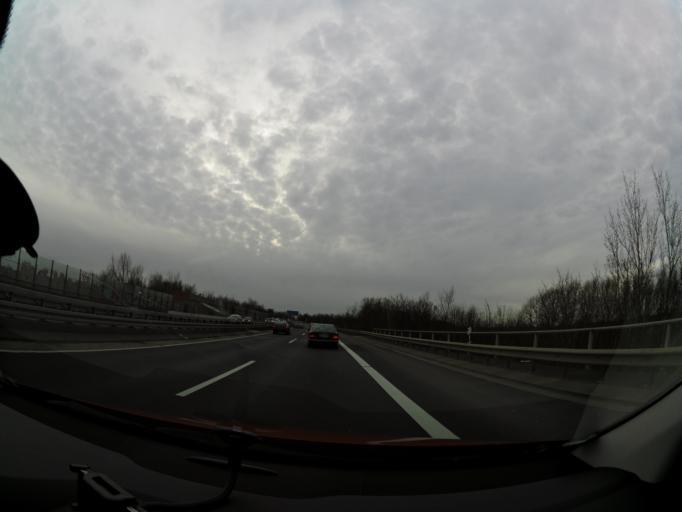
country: DE
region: Lower Saxony
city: Braunschweig
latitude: 52.2931
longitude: 10.4951
